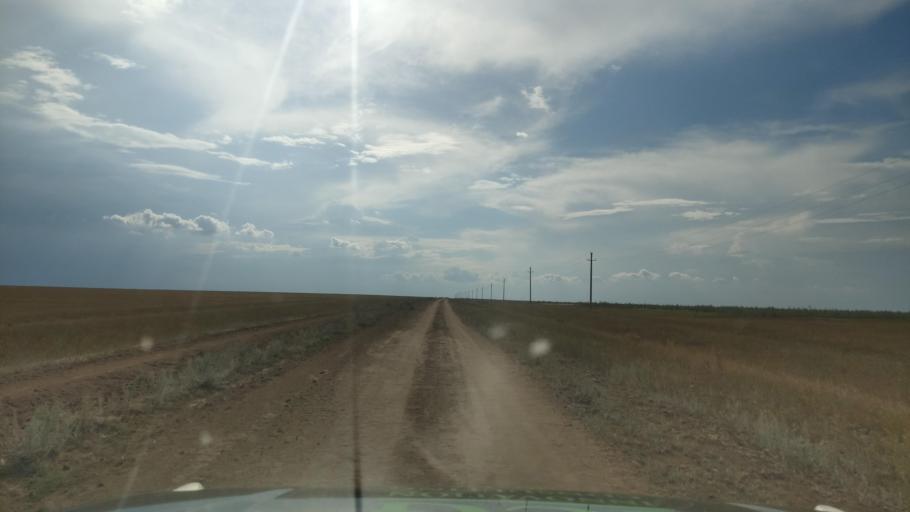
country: KZ
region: Pavlodar
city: Pavlodar
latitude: 52.5091
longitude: 77.5744
